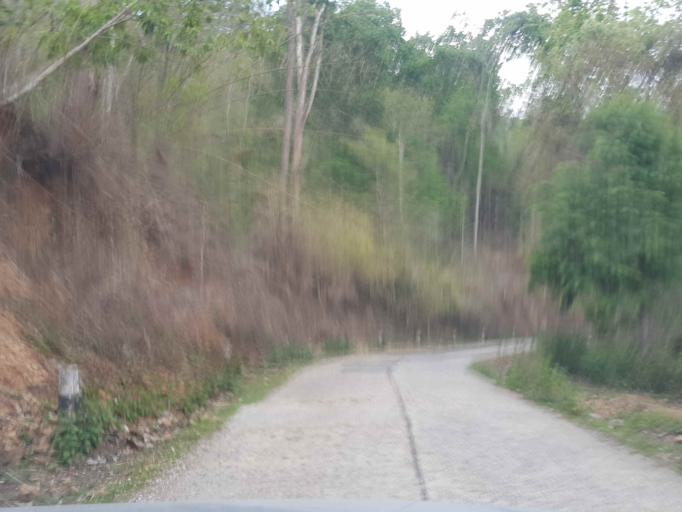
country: TH
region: Chiang Mai
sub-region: Amphoe Chiang Dao
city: Chiang Dao
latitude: 19.3802
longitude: 98.7687
